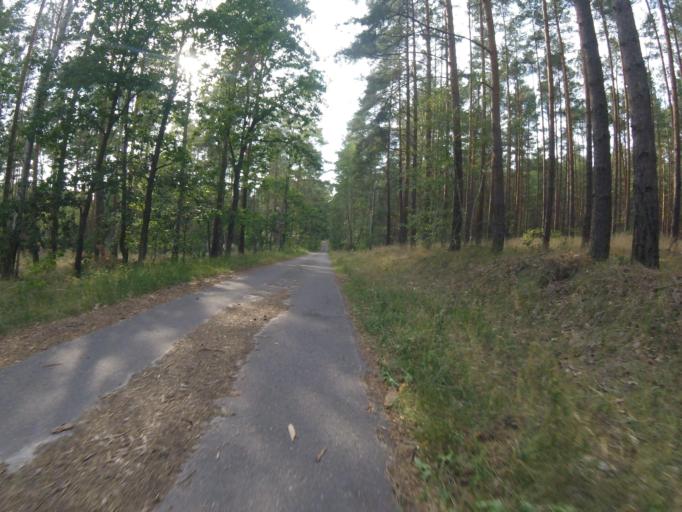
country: DE
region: Brandenburg
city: Gross Koris
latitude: 52.2110
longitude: 13.7114
